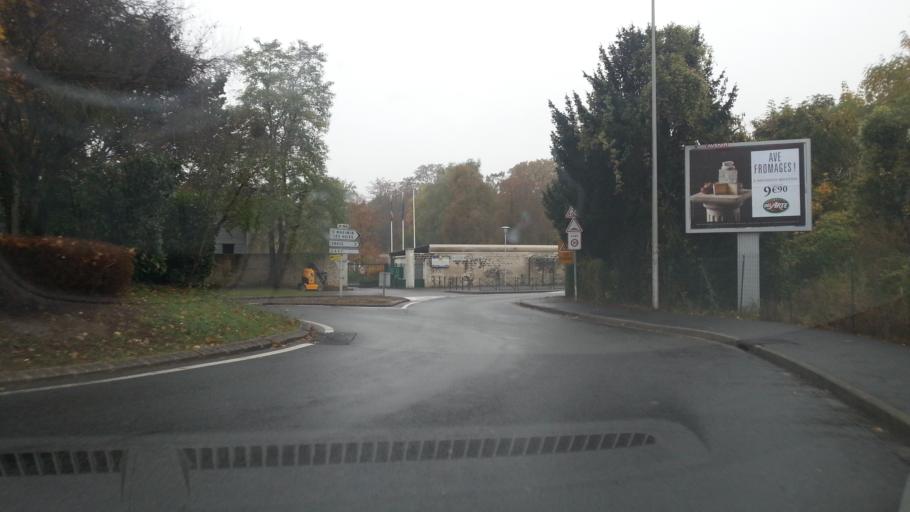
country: FR
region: Picardie
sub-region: Departement de l'Oise
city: Saint-Maximin
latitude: 49.2333
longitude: 2.4597
